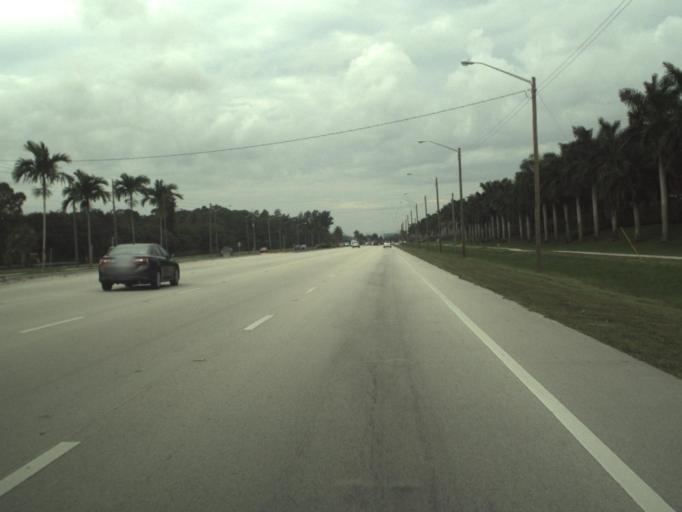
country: US
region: Florida
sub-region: Palm Beach County
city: Royal Palm Beach
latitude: 26.7092
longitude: -80.1914
